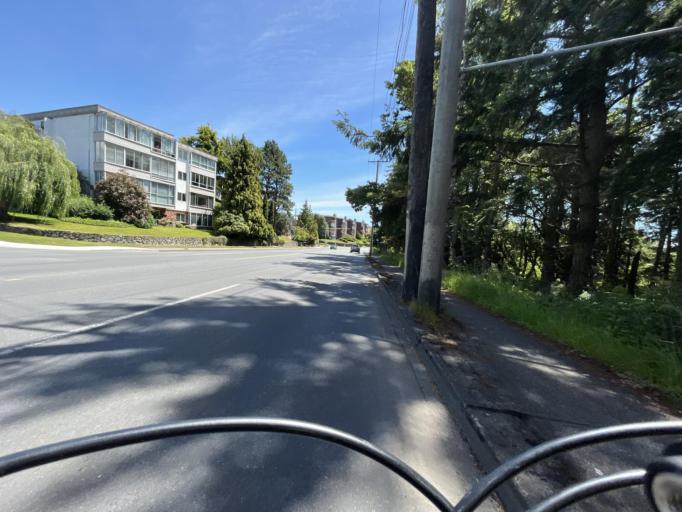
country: CA
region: British Columbia
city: Victoria
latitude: 48.4469
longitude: -123.3962
